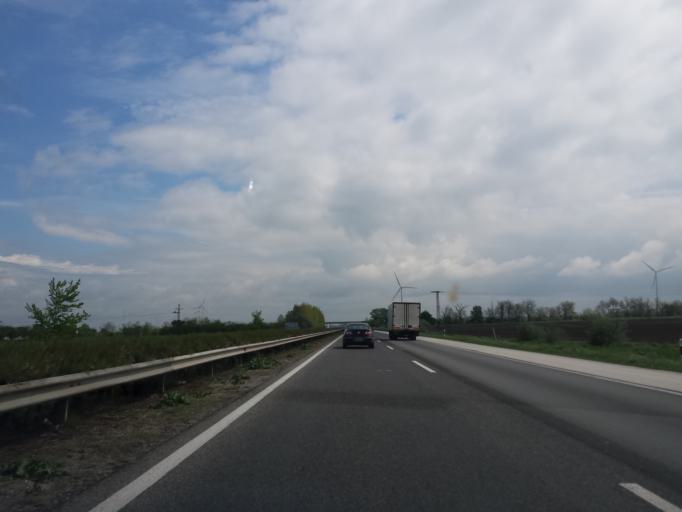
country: HU
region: Gyor-Moson-Sopron
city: Bony
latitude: 47.6806
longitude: 17.9116
